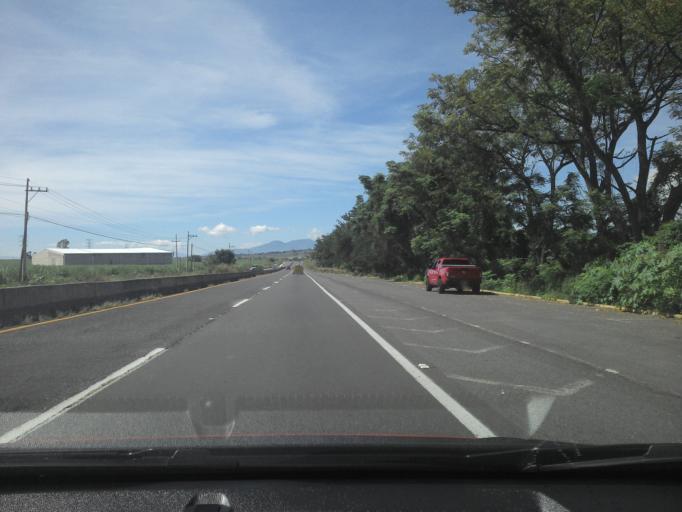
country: MX
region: Jalisco
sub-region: Tala
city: Los Ruisenores
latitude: 20.7080
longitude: -103.6741
